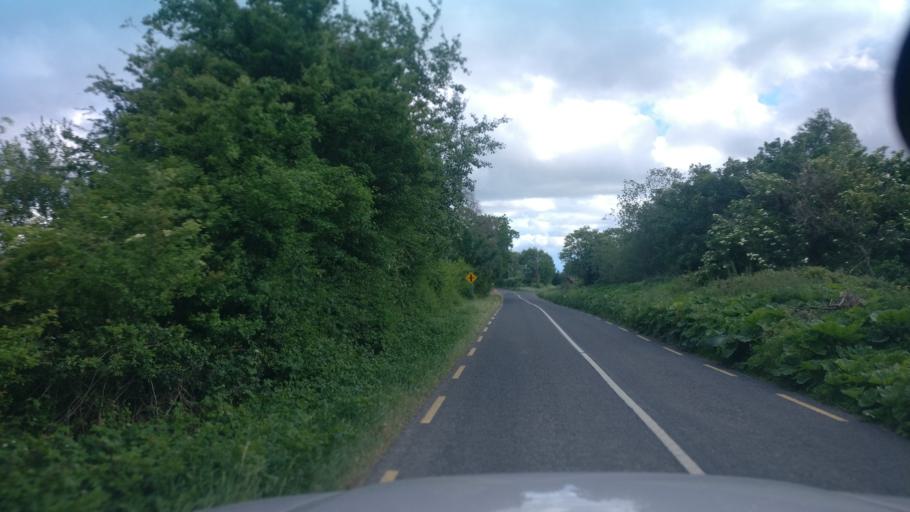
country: IE
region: Connaught
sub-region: County Galway
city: Portumna
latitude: 53.1973
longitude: -8.3032
